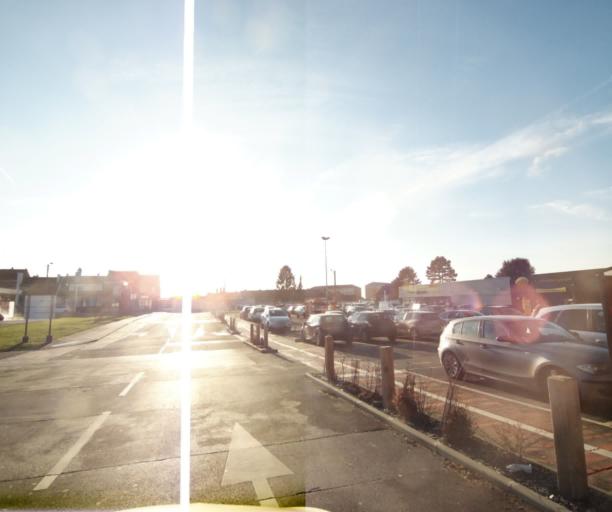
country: FR
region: Nord-Pas-de-Calais
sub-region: Departement du Nord
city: Marly
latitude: 50.3472
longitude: 3.5532
